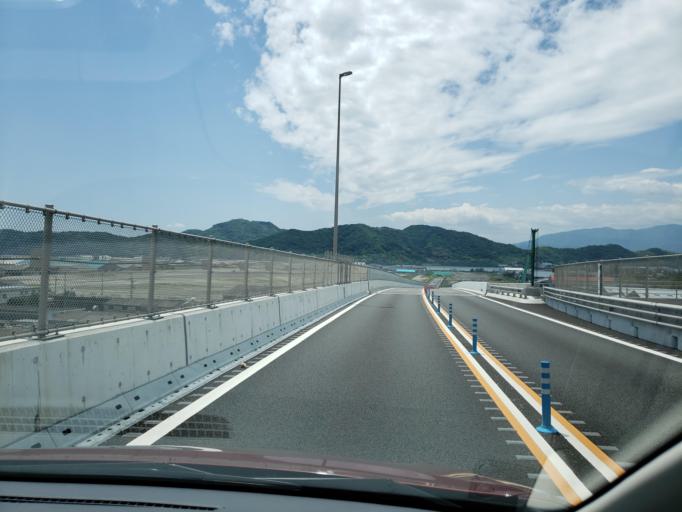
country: JP
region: Tokushima
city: Tokushima-shi
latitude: 34.0485
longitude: 134.5855
